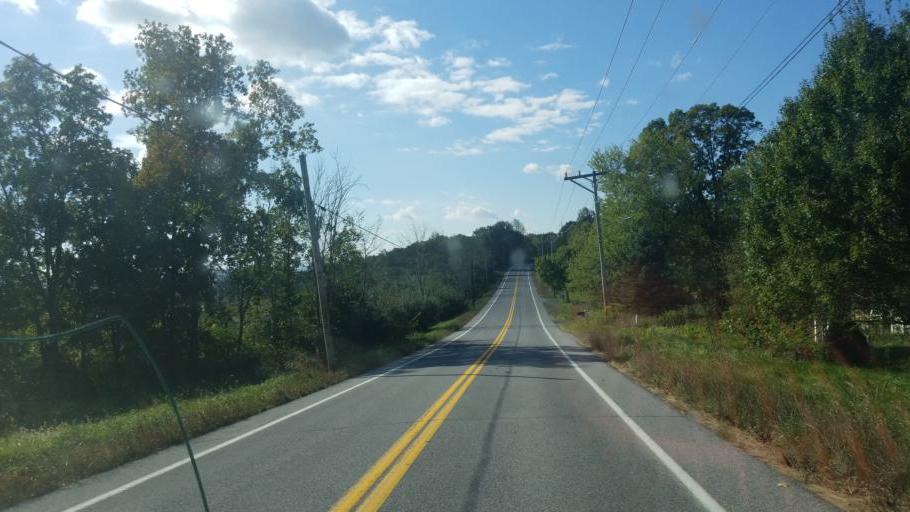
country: US
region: Pennsylvania
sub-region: Bedford County
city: Bedford
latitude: 40.1339
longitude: -78.5183
